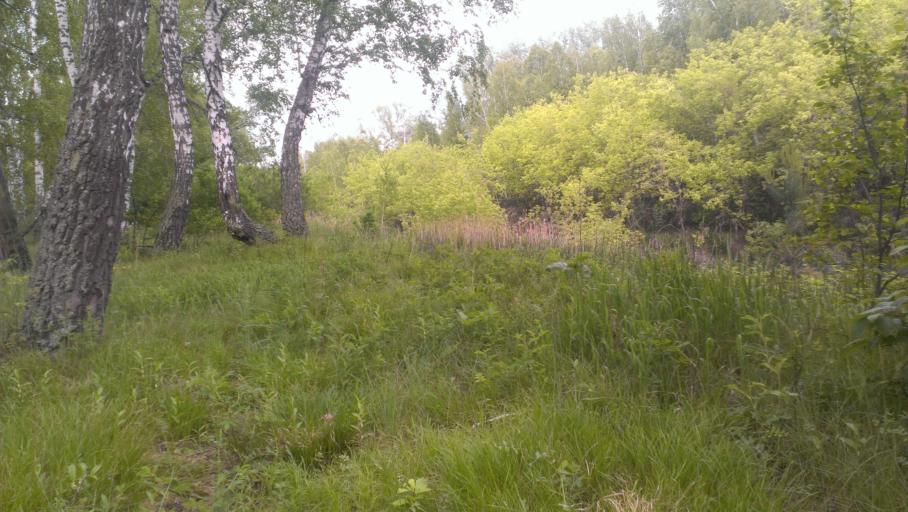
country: RU
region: Altai Krai
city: Sannikovo
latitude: 53.3412
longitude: 84.0584
